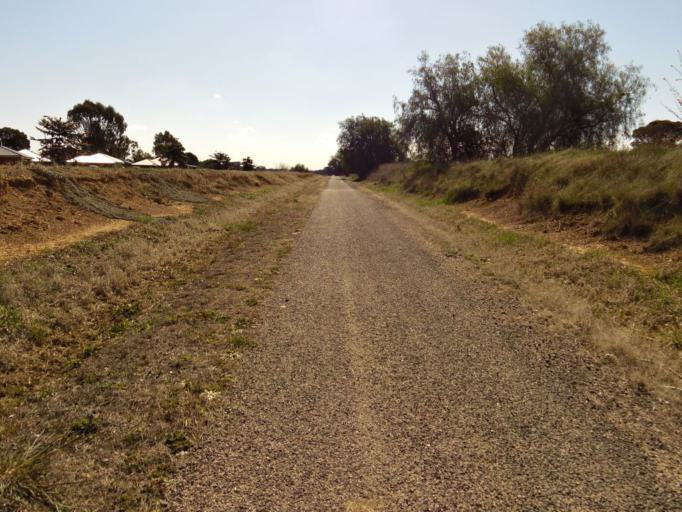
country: AU
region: New South Wales
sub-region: Corowa Shire
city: Corowa
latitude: -36.0514
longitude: 146.4609
